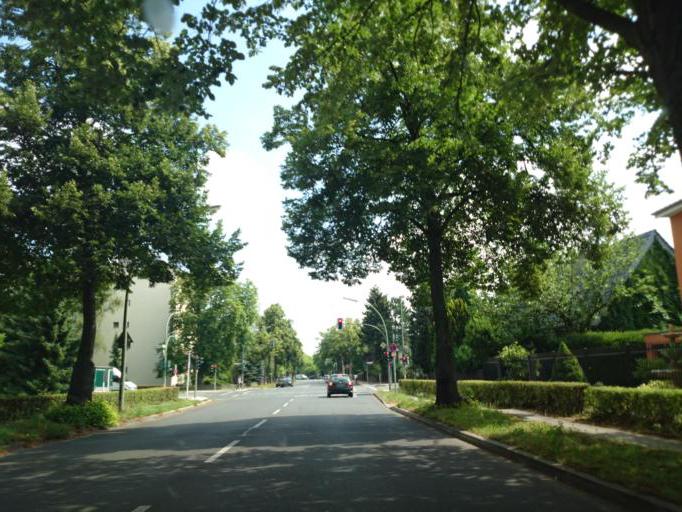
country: DE
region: Berlin
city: Zehlendorf Bezirk
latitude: 52.4316
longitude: 13.2769
